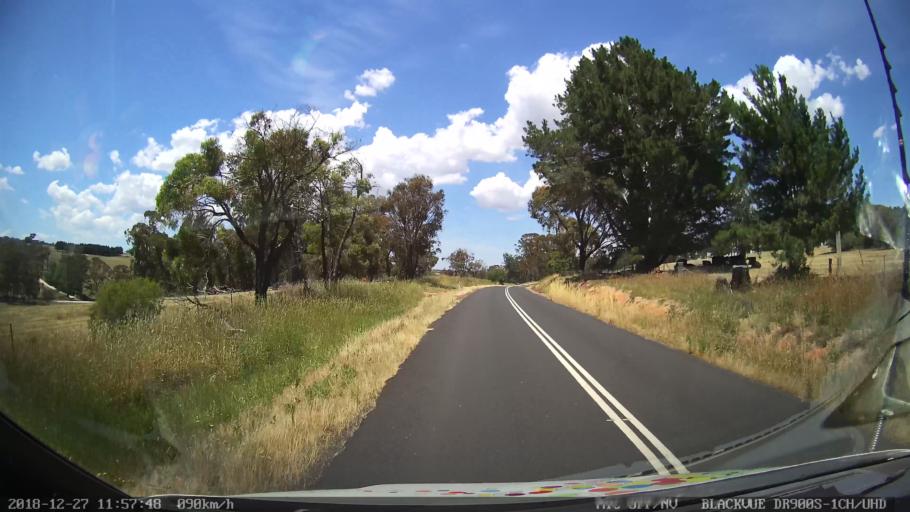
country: AU
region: New South Wales
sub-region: Blayney
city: Blayney
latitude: -33.7163
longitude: 149.3884
